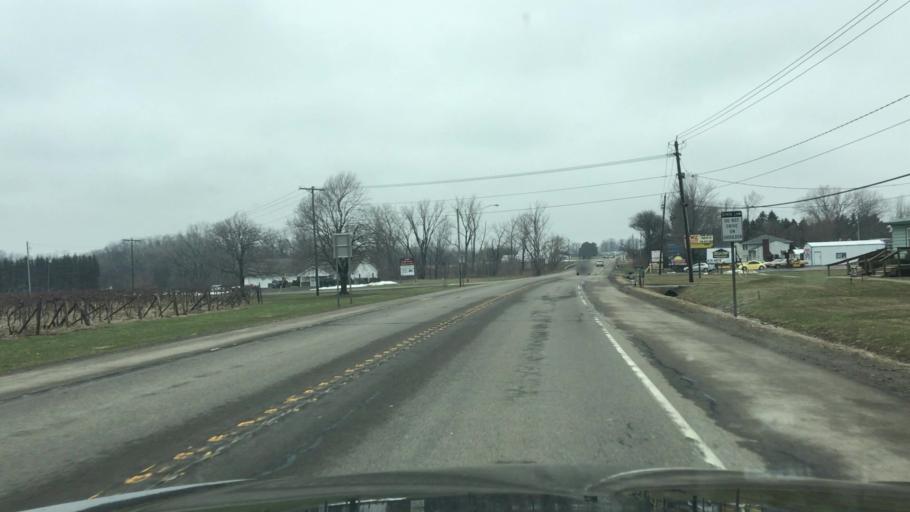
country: US
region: New York
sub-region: Chautauqua County
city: Fredonia
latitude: 42.4295
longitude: -79.3067
